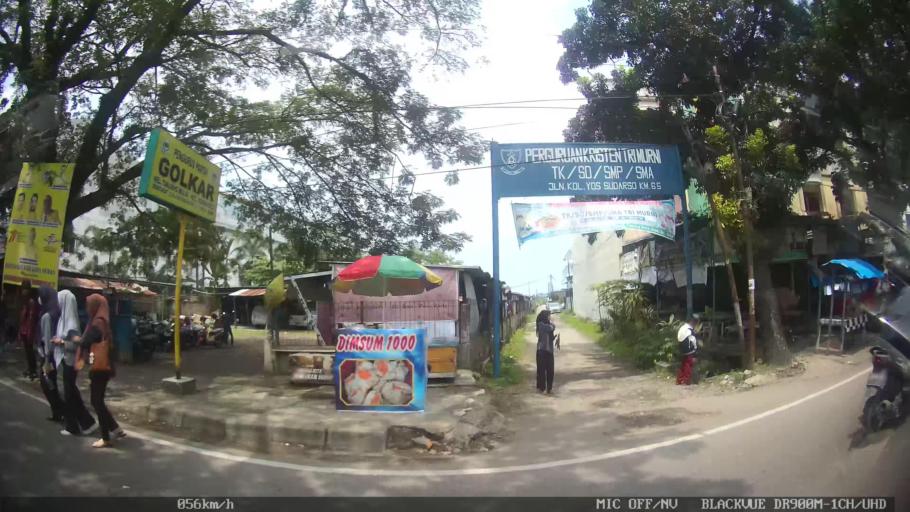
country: ID
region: North Sumatra
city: Medan
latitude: 3.6376
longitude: 98.6660
